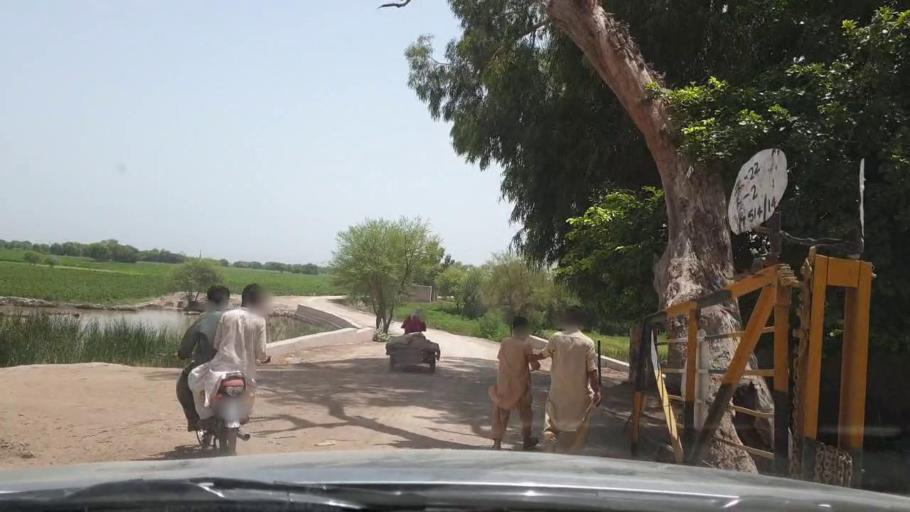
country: PK
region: Sindh
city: Pano Aqil
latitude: 27.8847
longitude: 69.1434
